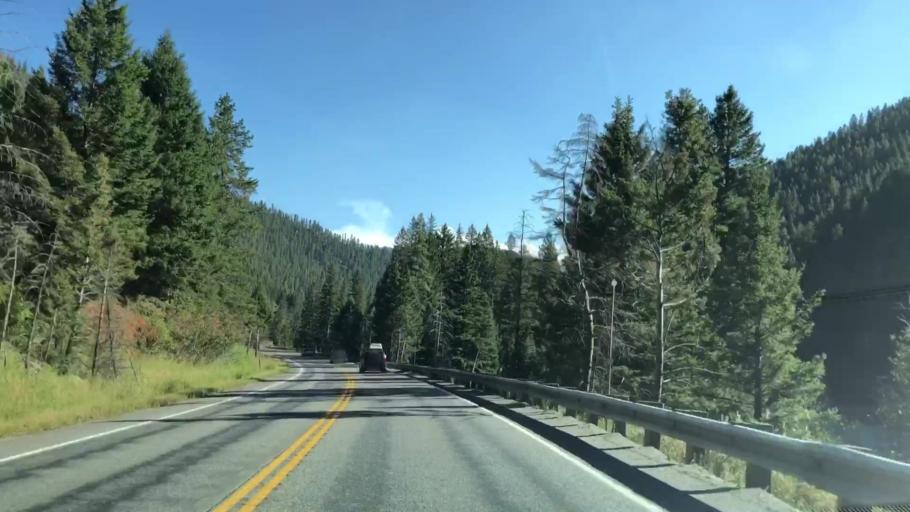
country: US
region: Montana
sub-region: Gallatin County
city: Big Sky
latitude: 45.3656
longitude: -111.1748
